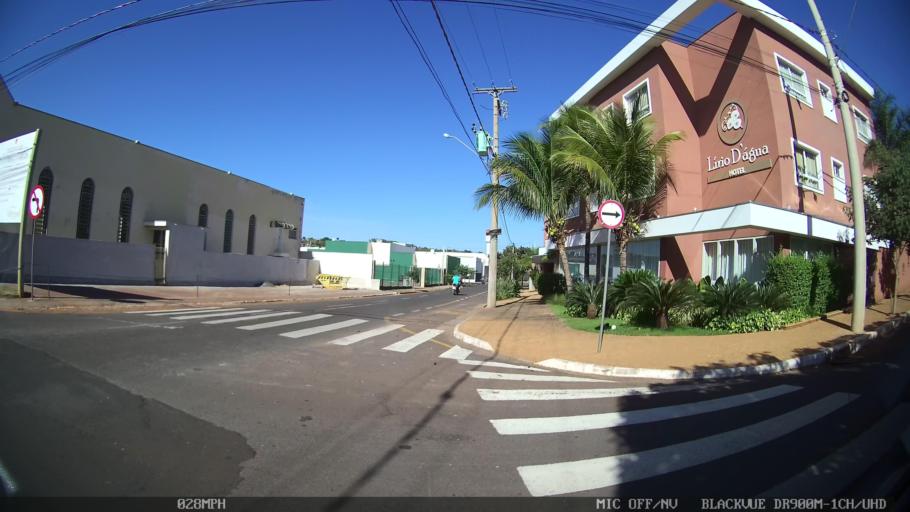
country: BR
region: Sao Paulo
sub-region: Olimpia
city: Olimpia
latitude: -20.7304
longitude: -48.9154
